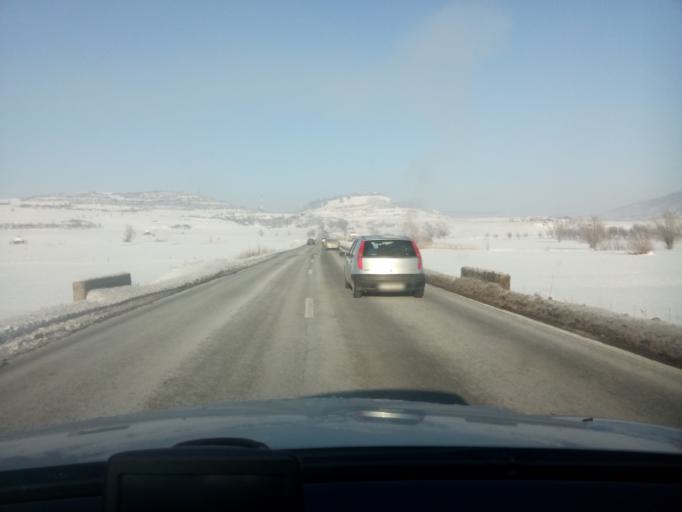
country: RO
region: Sibiu
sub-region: Comuna Boita
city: Boita
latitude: 45.6393
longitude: 24.2611
